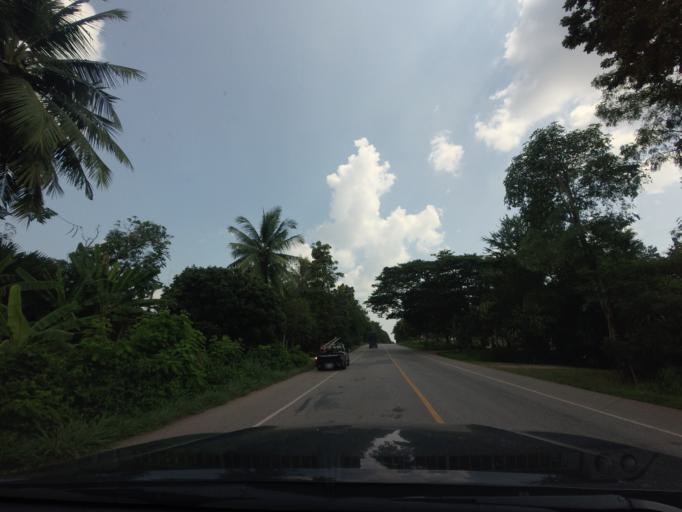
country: TH
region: Phitsanulok
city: Chat Trakan
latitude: 17.2800
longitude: 100.5373
